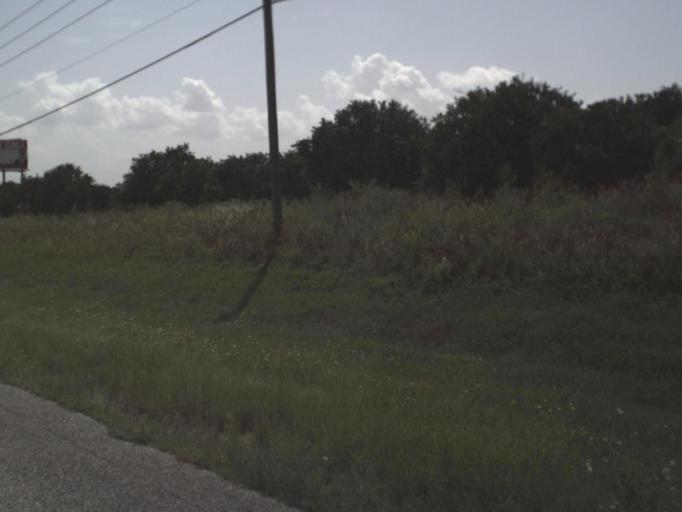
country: US
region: Florida
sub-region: Polk County
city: Davenport
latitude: 28.1997
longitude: -81.6400
